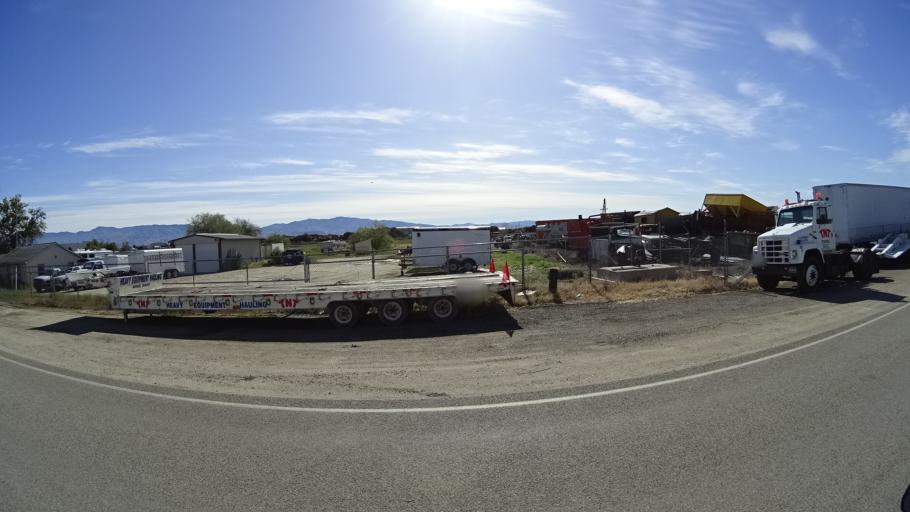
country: US
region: Idaho
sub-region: Ada County
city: Garden City
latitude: 43.5669
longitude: -116.2598
